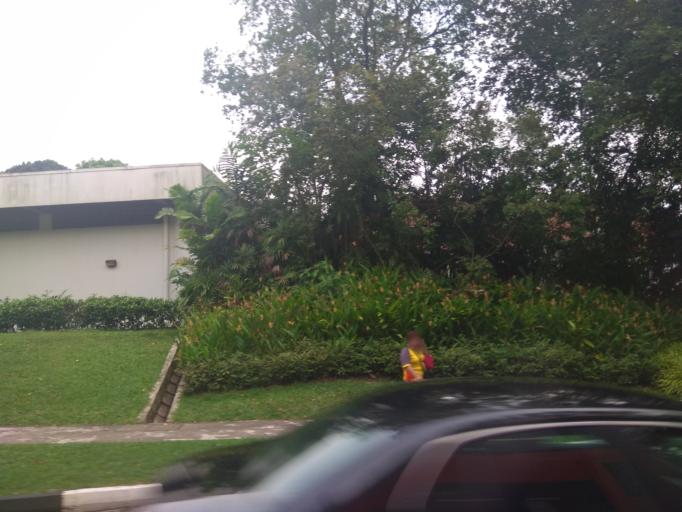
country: MY
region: Johor
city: Johor Bahru
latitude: 1.3561
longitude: 103.6895
